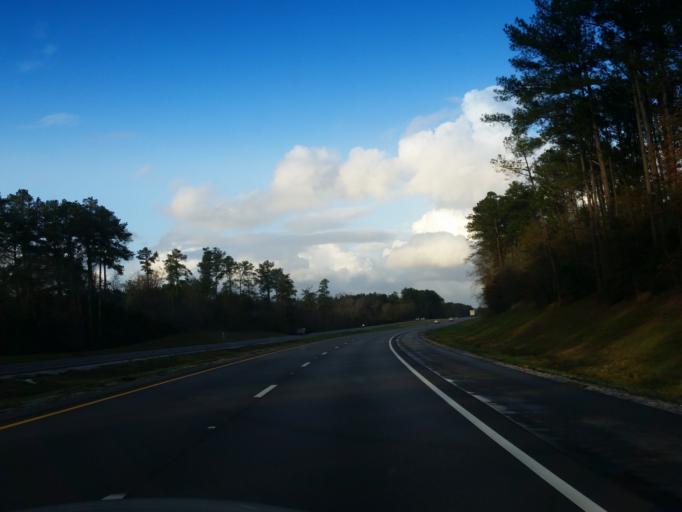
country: US
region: Mississippi
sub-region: Jones County
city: Sharon
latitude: 31.8738
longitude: -89.0450
